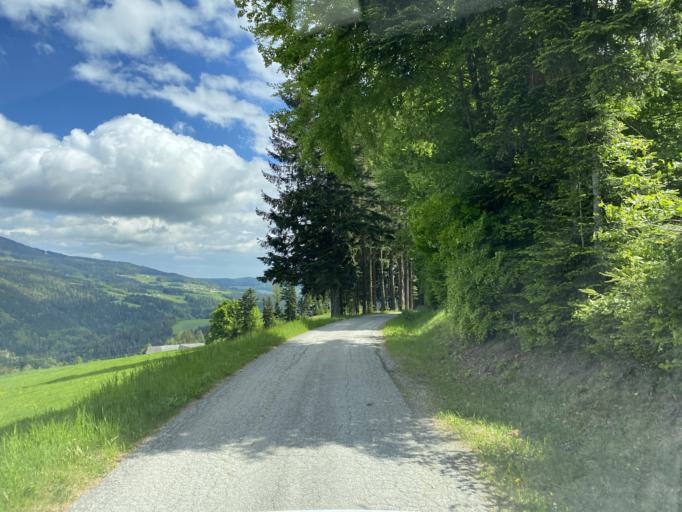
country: AT
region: Styria
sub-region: Politischer Bezirk Weiz
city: Koglhof
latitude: 47.3196
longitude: 15.6731
